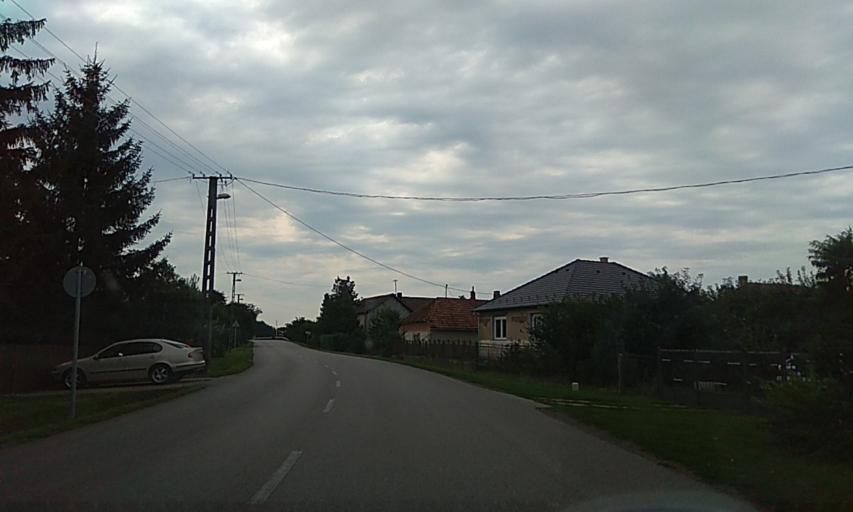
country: HU
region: Szabolcs-Szatmar-Bereg
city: Buj
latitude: 48.0944
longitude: 21.6410
